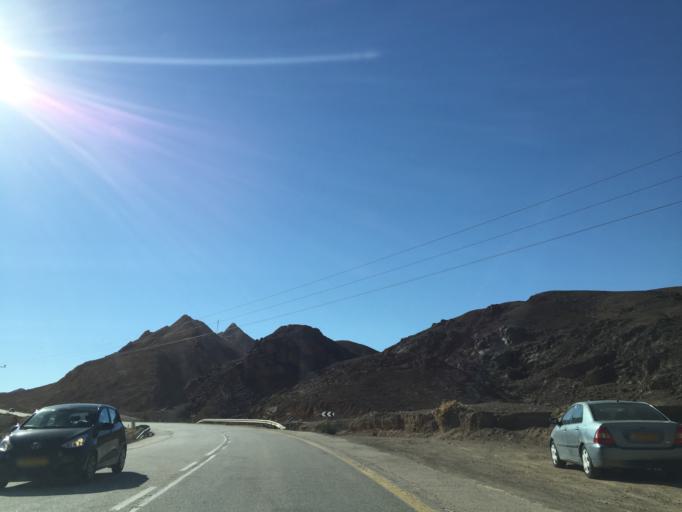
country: IL
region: Southern District
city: Mitzpe Ramon
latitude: 30.5850
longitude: 34.8895
